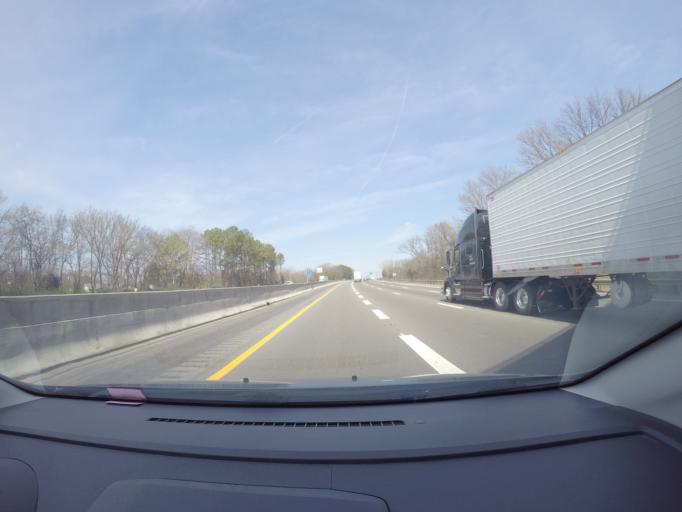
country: US
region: Tennessee
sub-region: Rutherford County
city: La Vergne
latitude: 36.0537
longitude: -86.6730
